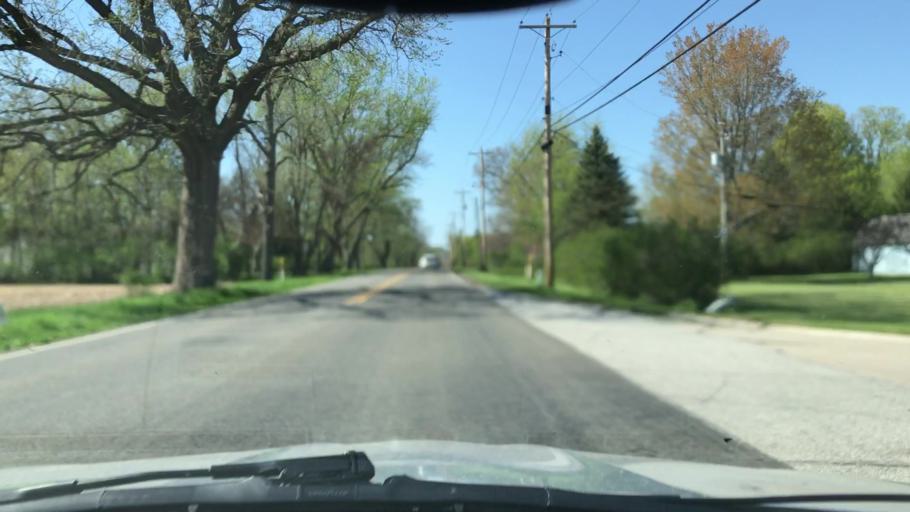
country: US
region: Indiana
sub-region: Saint Joseph County
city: Georgetown
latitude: 41.7477
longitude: -86.2991
